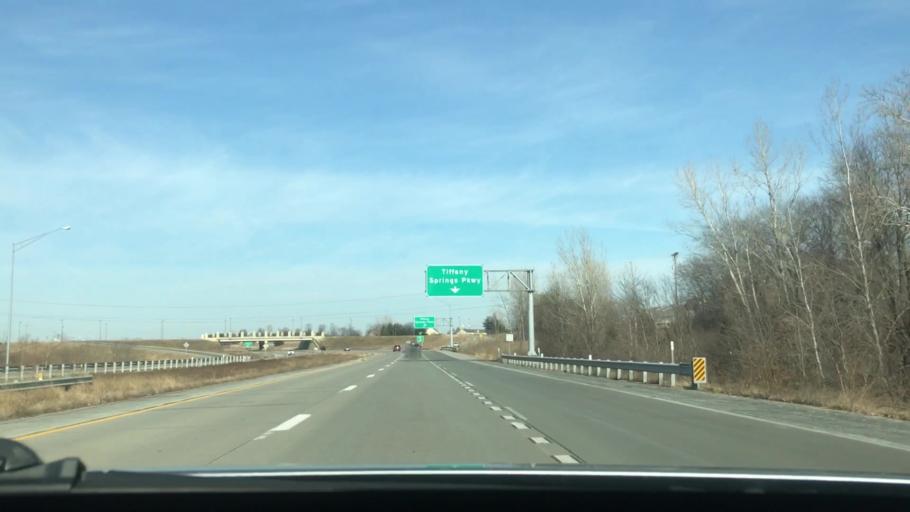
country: US
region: Missouri
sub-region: Clay County
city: Gladstone
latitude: 39.2654
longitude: -94.5855
